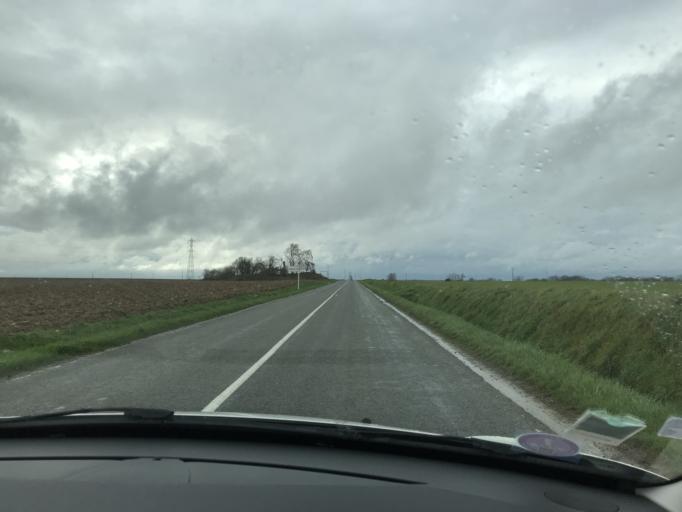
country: FR
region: Picardie
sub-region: Departement de l'Aisne
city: Billy-sur-Aisne
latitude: 49.3424
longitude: 3.3796
